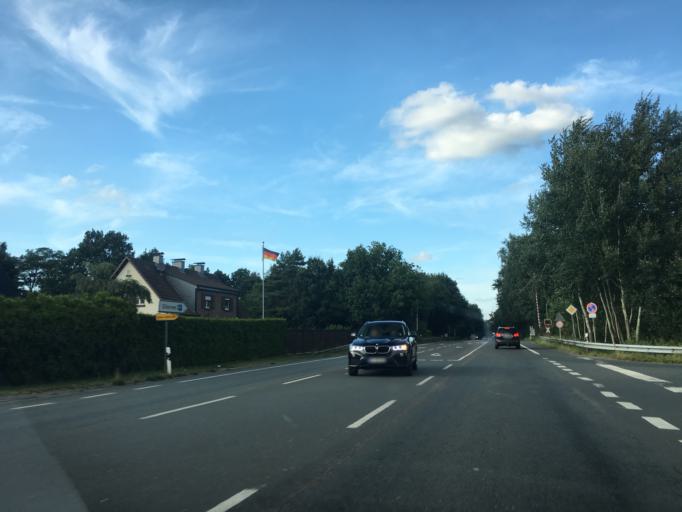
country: DE
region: North Rhine-Westphalia
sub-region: Regierungsbezirk Munster
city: Haltern
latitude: 51.7897
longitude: 7.2227
